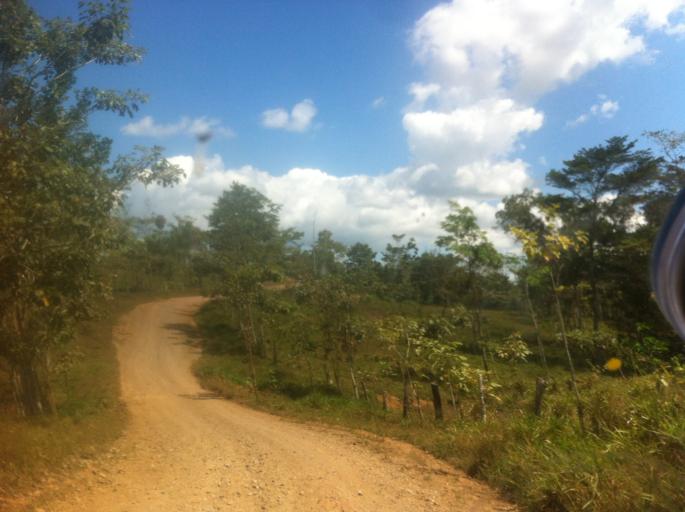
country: CR
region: Alajuela
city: Los Chiles
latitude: 11.2494
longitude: -84.4608
